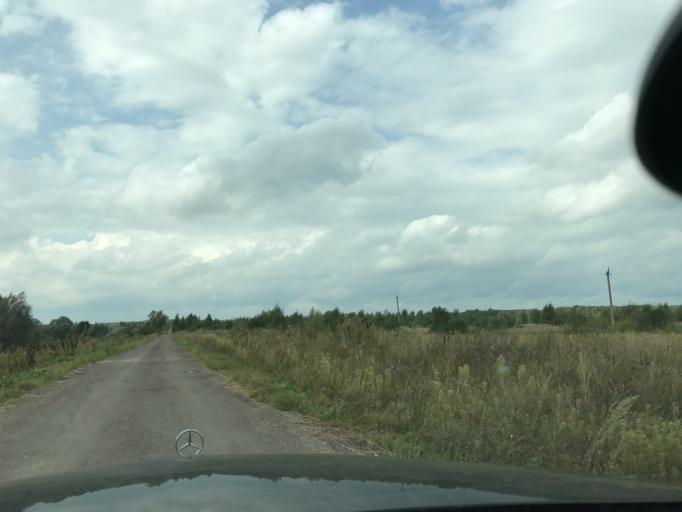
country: RU
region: Nizjnij Novgorod
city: Vacha
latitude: 55.9787
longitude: 42.7734
